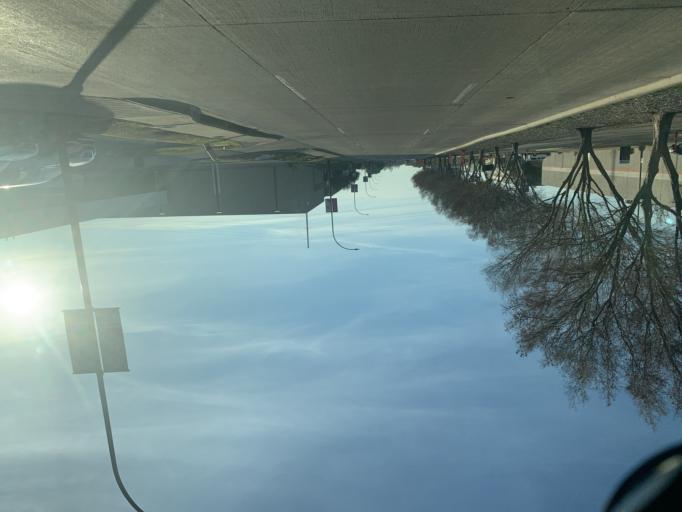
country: US
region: Texas
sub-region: Tarrant County
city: Arlington
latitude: 32.7479
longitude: -97.0758
